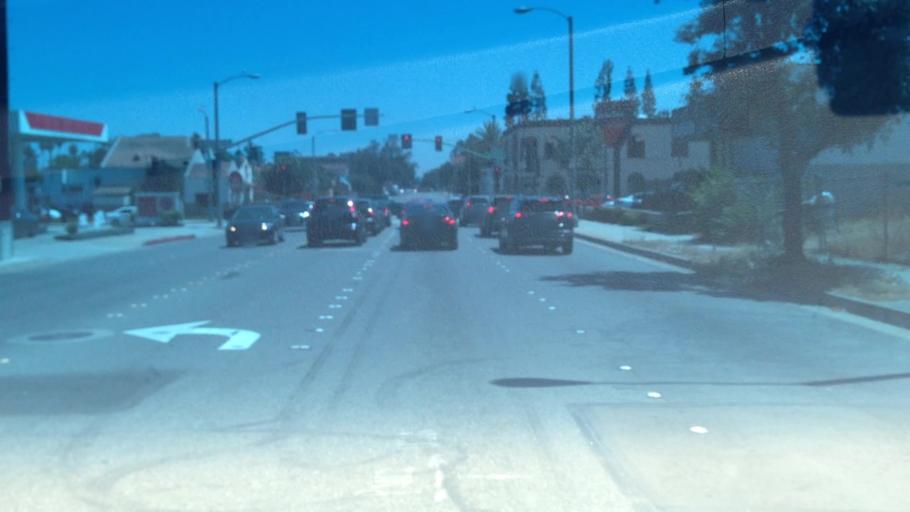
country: US
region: California
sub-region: Los Angeles County
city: Pasadena
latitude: 34.1503
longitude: -118.1215
